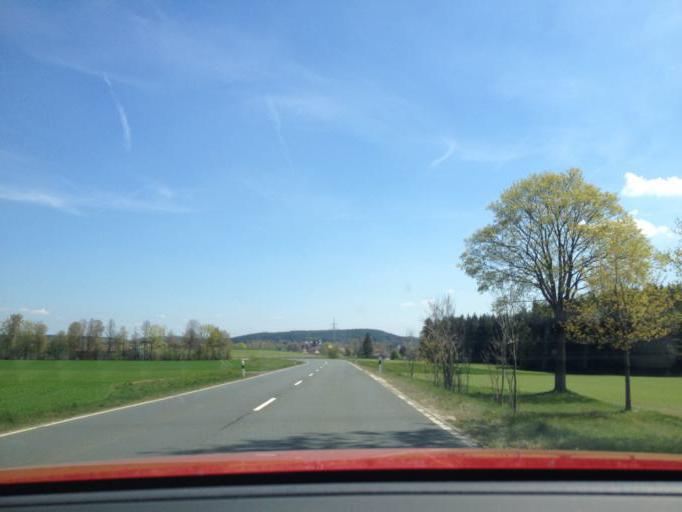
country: DE
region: Bavaria
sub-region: Upper Franconia
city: Marktleuthen
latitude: 50.1330
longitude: 11.9794
